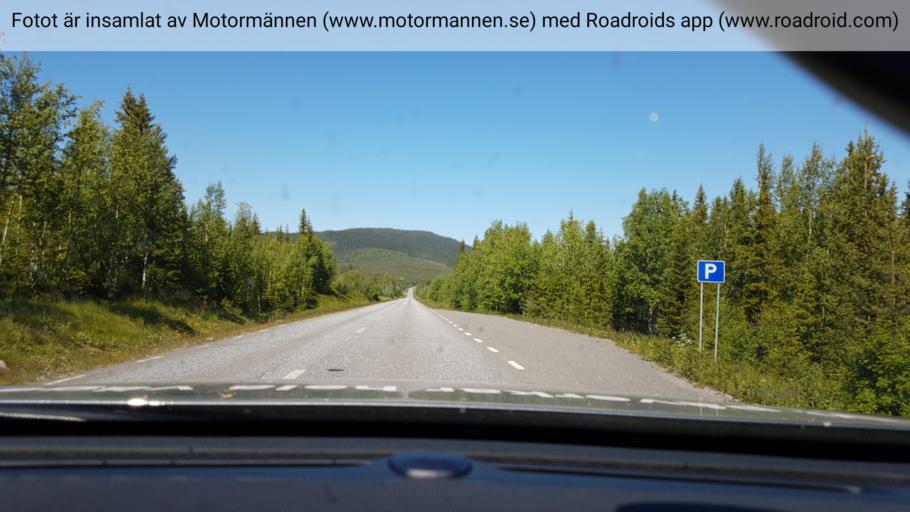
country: SE
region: Vaesterbotten
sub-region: Vilhelmina Kommun
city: Sjoberg
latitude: 64.8837
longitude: 15.8661
